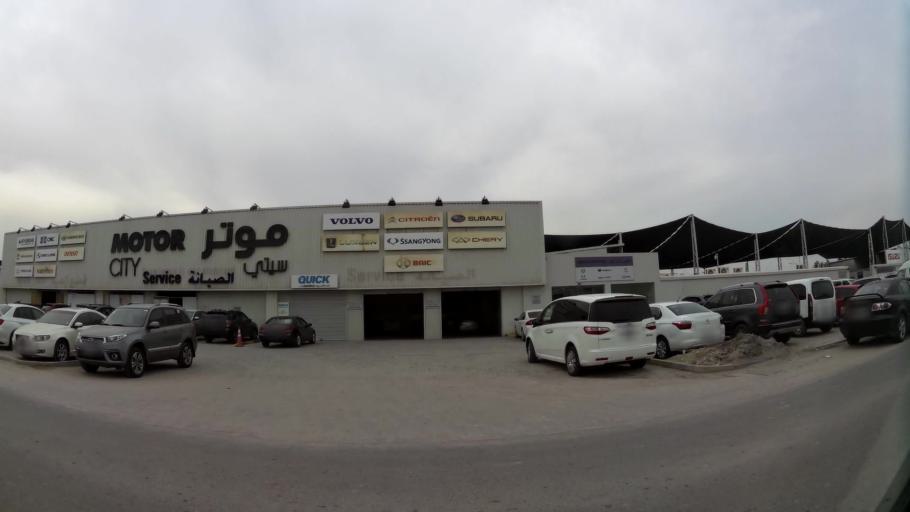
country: BH
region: Northern
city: Sitrah
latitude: 26.1270
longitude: 50.6023
